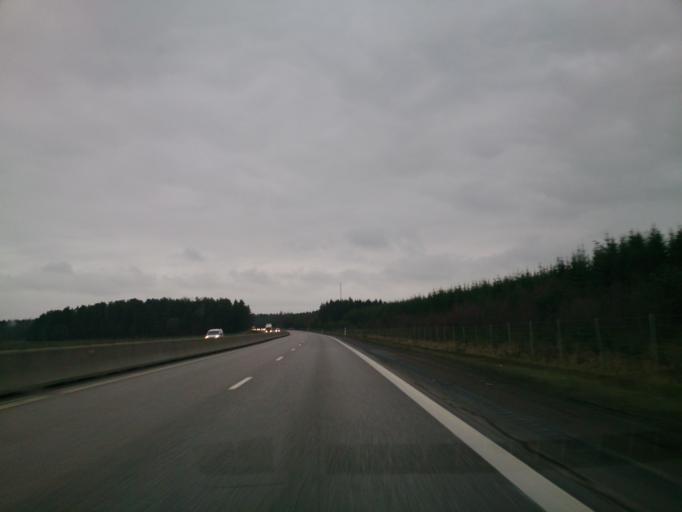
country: SE
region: OEstergoetland
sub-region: Norrkopings Kommun
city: Kimstad
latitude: 58.4956
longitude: 15.9737
